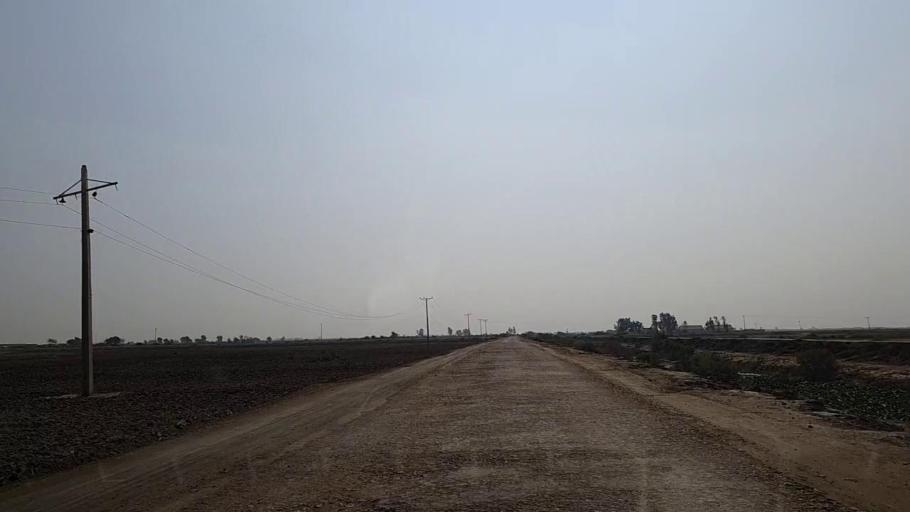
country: PK
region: Sindh
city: Thatta
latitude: 24.7143
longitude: 67.7684
